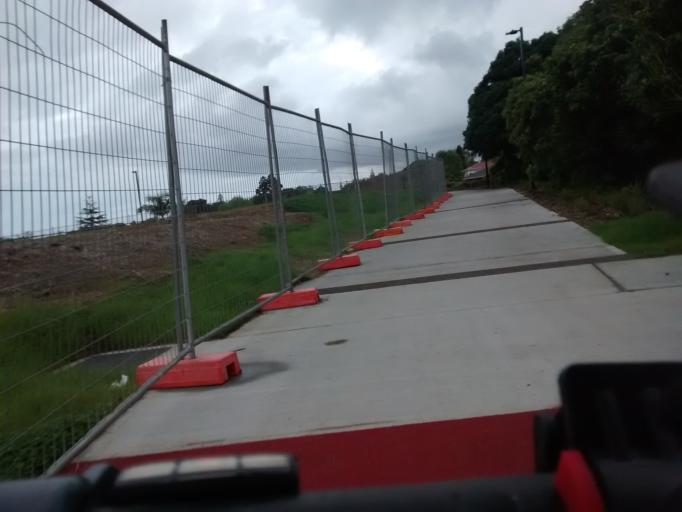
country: NZ
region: Auckland
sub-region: Auckland
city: Rosebank
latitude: -36.8849
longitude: 174.7043
